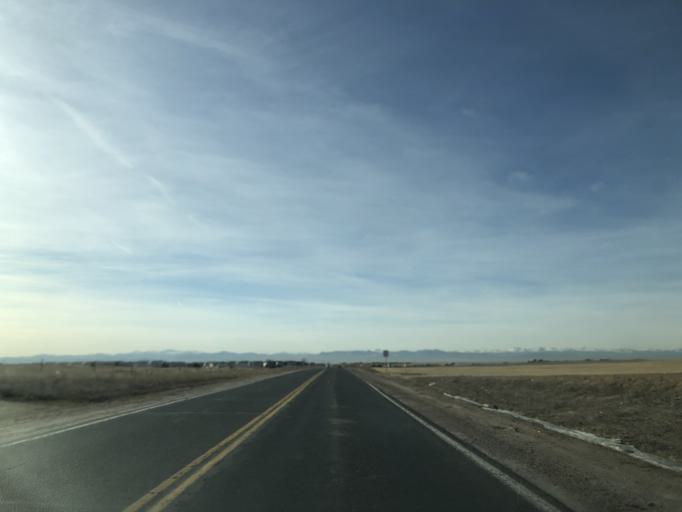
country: US
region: Colorado
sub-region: Adams County
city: Aurora
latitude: 39.7985
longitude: -104.7271
